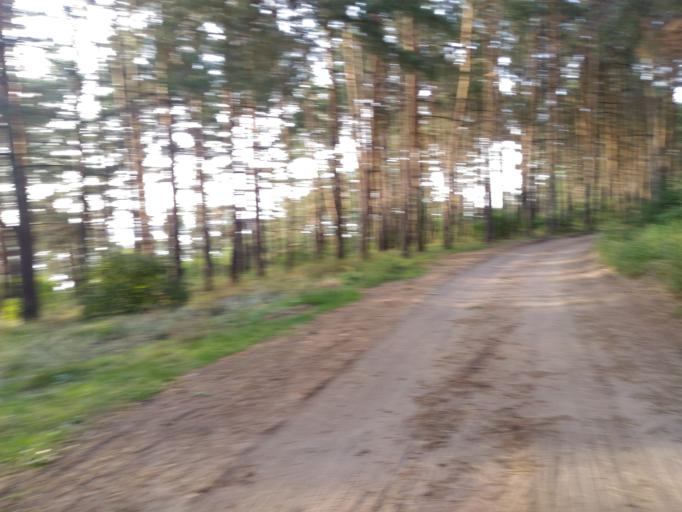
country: RU
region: Ulyanovsk
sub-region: Ulyanovskiy Rayon
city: Ulyanovsk
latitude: 54.3590
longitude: 48.5131
